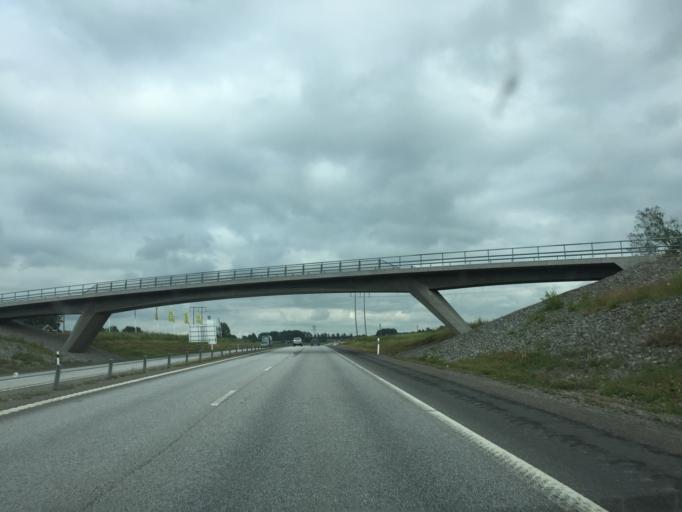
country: SE
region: OErebro
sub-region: Orebro Kommun
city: Vintrosa
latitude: 59.2456
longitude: 14.9727
